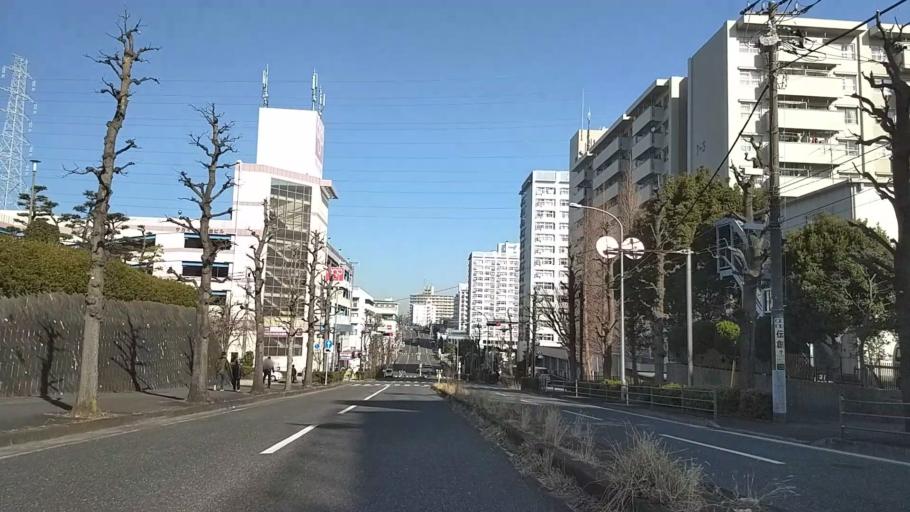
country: JP
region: Kanagawa
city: Kamakura
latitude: 35.3764
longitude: 139.5966
